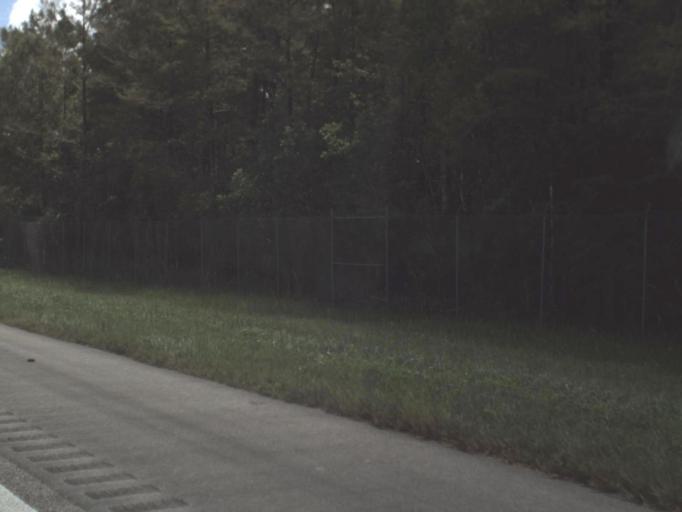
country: US
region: Florida
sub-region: Collier County
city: Orangetree
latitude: 26.1537
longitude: -81.4007
